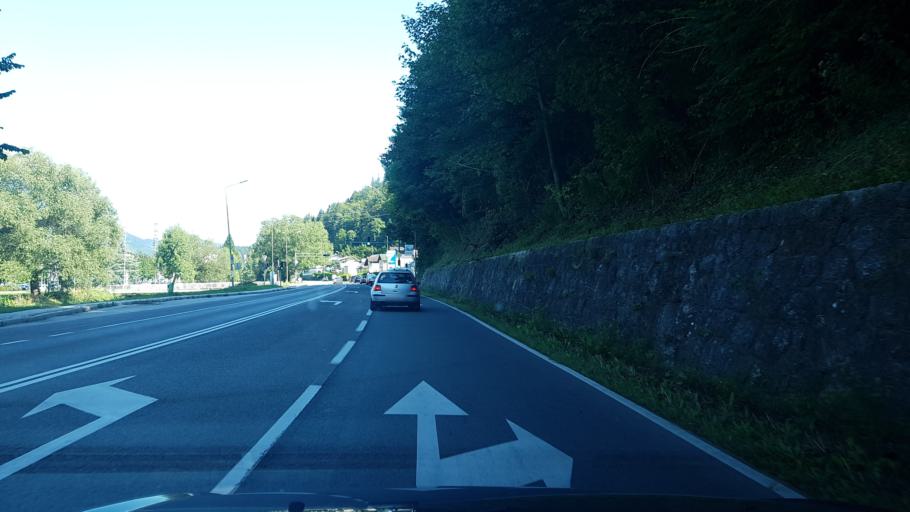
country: SI
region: Velenje
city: Velenje
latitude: 46.3603
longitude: 15.0973
